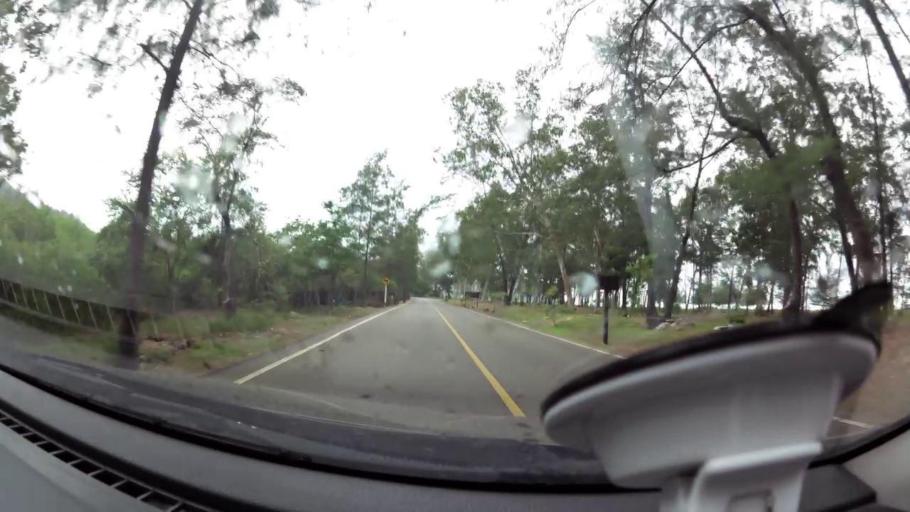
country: TH
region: Prachuap Khiri Khan
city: Pran Buri
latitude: 12.4178
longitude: 99.9842
